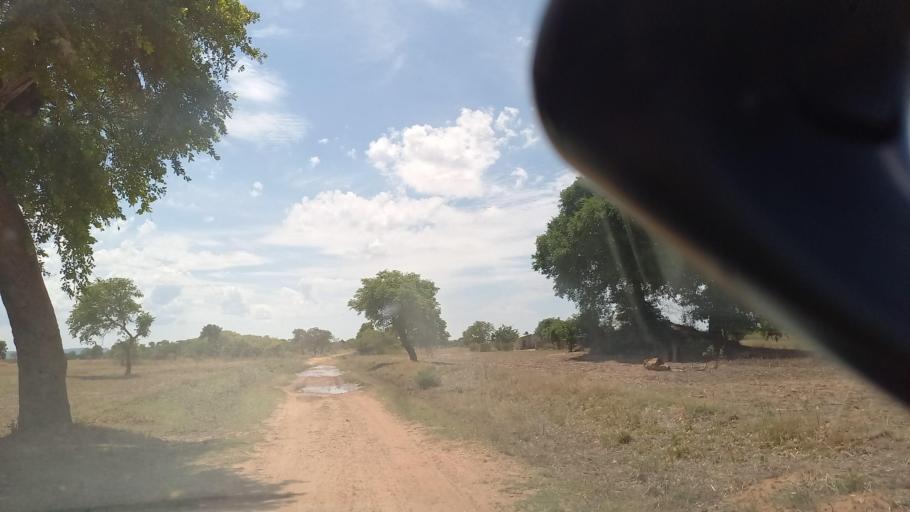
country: ZM
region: Southern
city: Mazabuka
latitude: -16.1454
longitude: 27.7729
